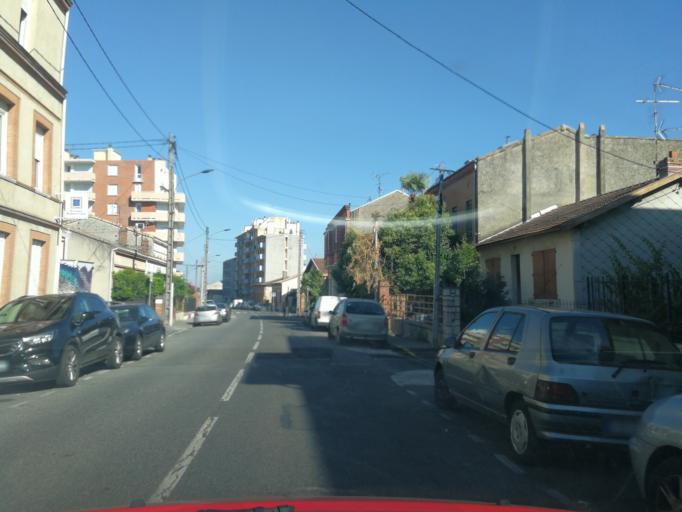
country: FR
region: Midi-Pyrenees
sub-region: Departement de la Haute-Garonne
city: Toulouse
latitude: 43.6225
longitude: 1.4632
